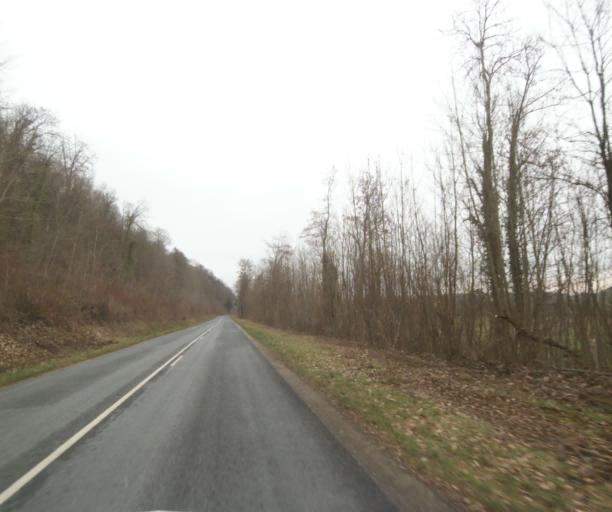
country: FR
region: Champagne-Ardenne
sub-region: Departement de la Haute-Marne
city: Bienville
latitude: 48.5726
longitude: 5.0376
